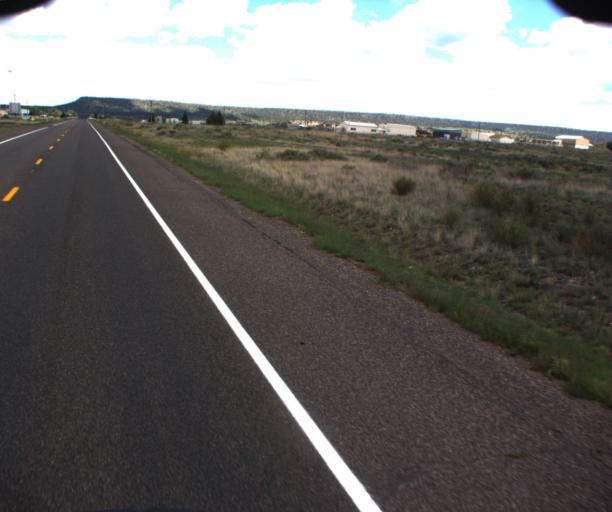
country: US
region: Arizona
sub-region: Apache County
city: Springerville
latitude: 34.1328
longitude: -109.2646
